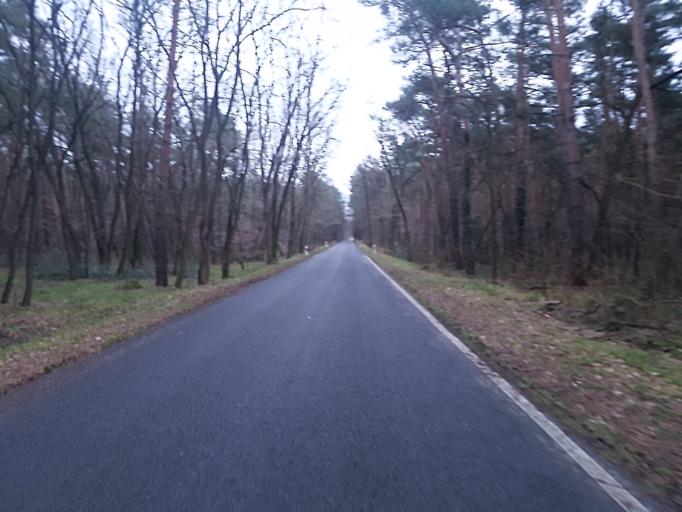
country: DE
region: Brandenburg
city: Schilda
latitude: 51.5843
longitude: 13.3926
